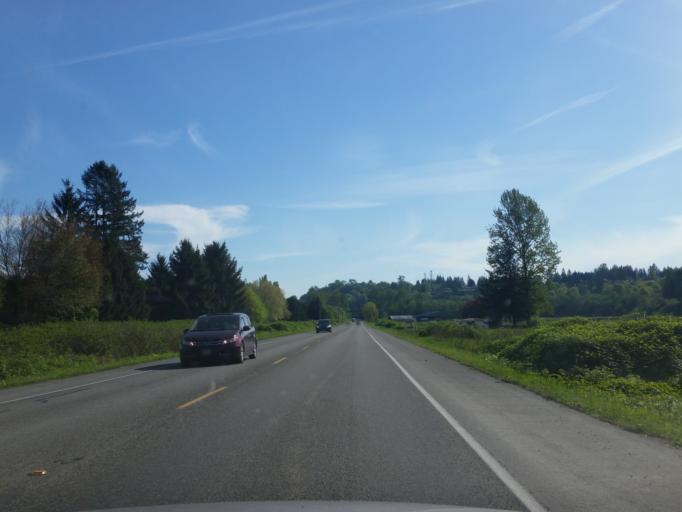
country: US
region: Washington
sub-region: Snohomish County
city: Machias
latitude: 47.9520
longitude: -122.0724
